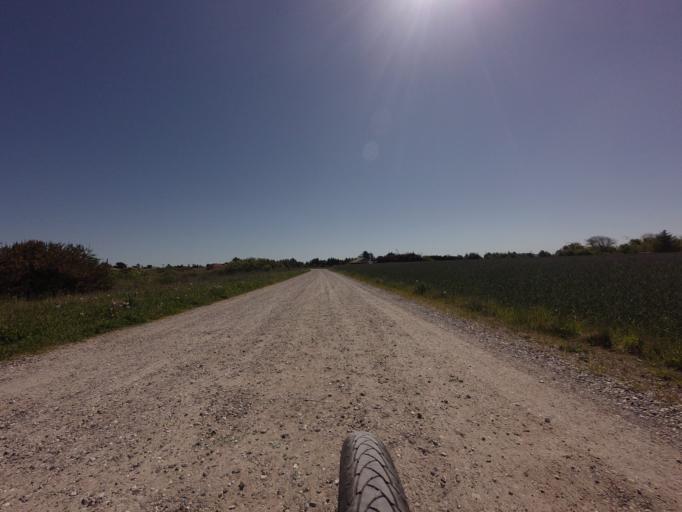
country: DK
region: North Denmark
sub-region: Jammerbugt Kommune
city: Pandrup
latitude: 57.2519
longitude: 9.6205
